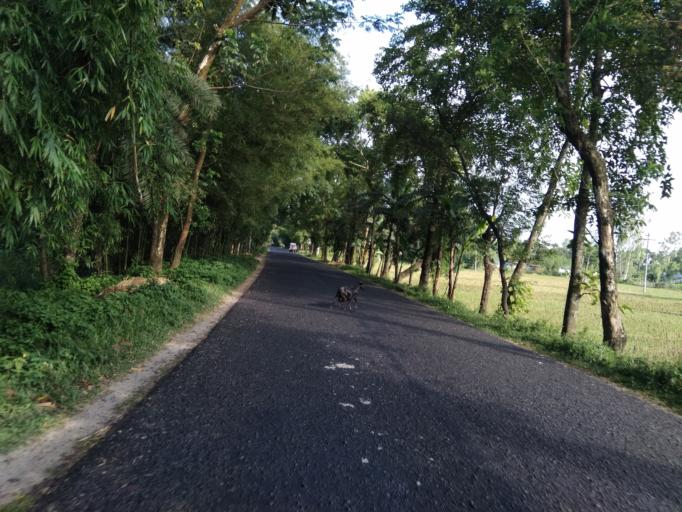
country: BD
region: Rangpur Division
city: Rangpur
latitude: 25.8343
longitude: 89.1161
